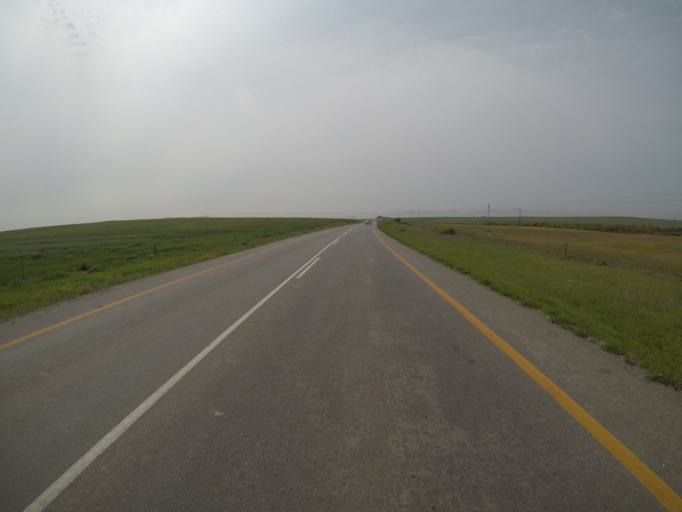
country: ZA
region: Western Cape
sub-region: City of Cape Town
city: Kraaifontein
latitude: -33.6967
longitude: 18.7096
